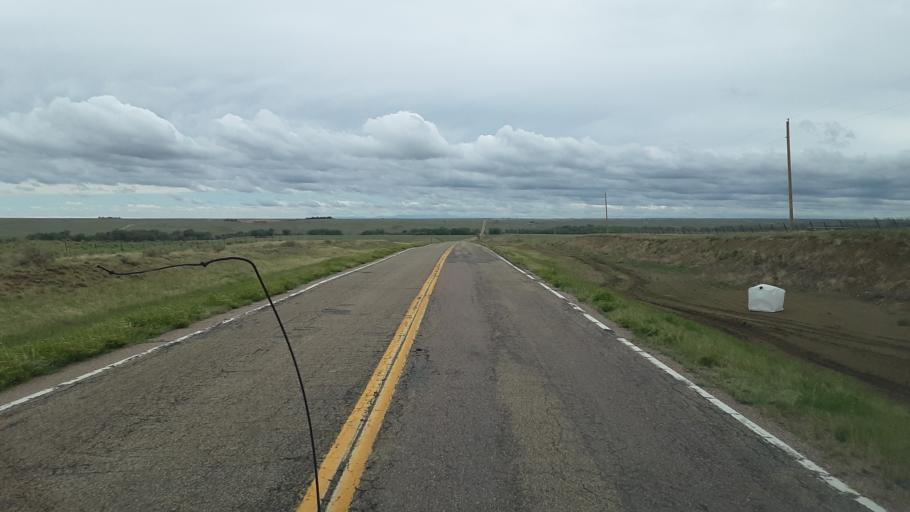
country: US
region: Colorado
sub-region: Lincoln County
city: Limon
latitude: 38.8378
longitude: -103.8248
